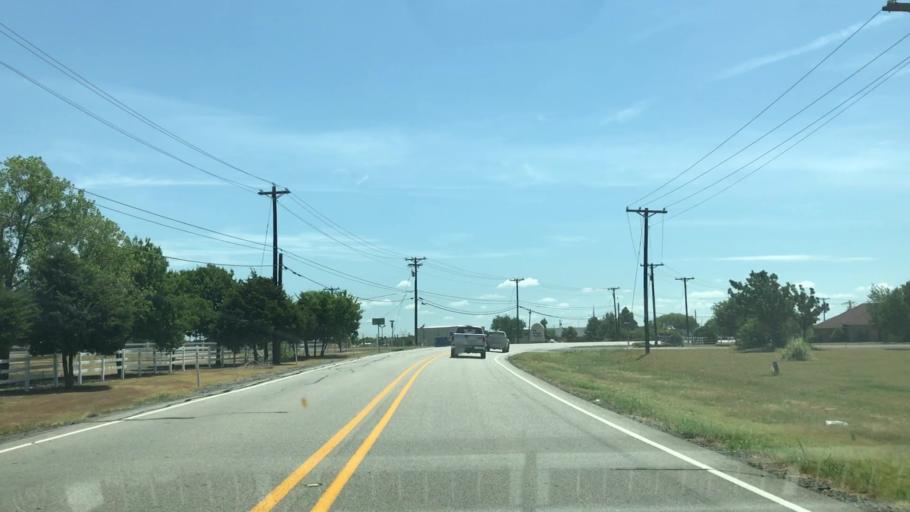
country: US
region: Texas
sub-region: Collin County
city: Saint Paul
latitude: 33.0343
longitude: -96.5487
